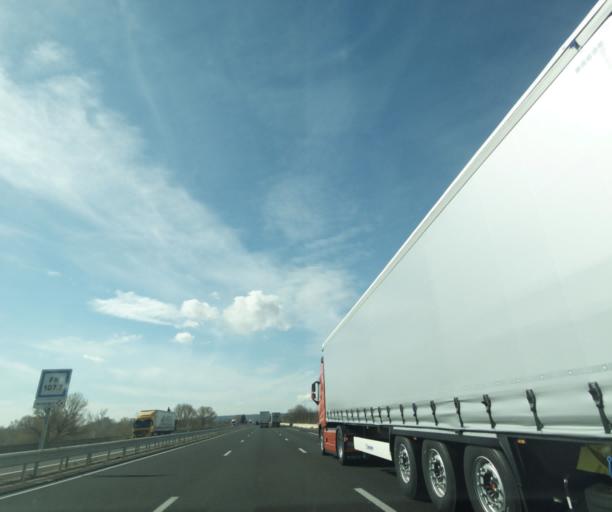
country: FR
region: Languedoc-Roussillon
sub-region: Departement du Gard
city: Remoulins
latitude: 43.9227
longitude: 4.5848
